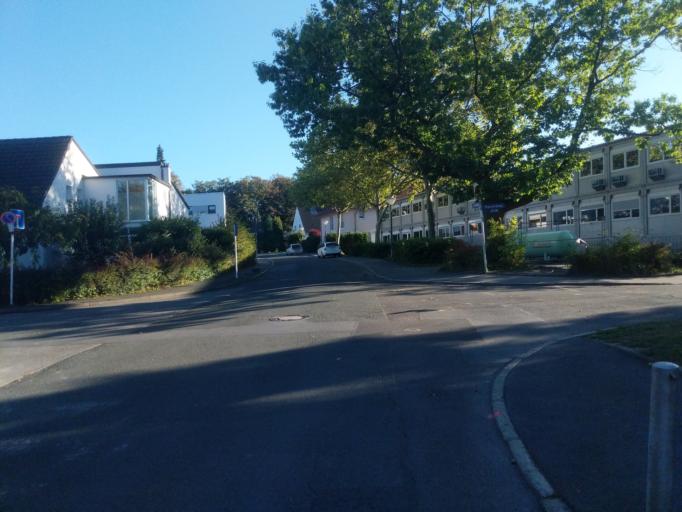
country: DE
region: North Rhine-Westphalia
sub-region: Regierungsbezirk Arnsberg
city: Dortmund
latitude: 51.4799
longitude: 7.4570
